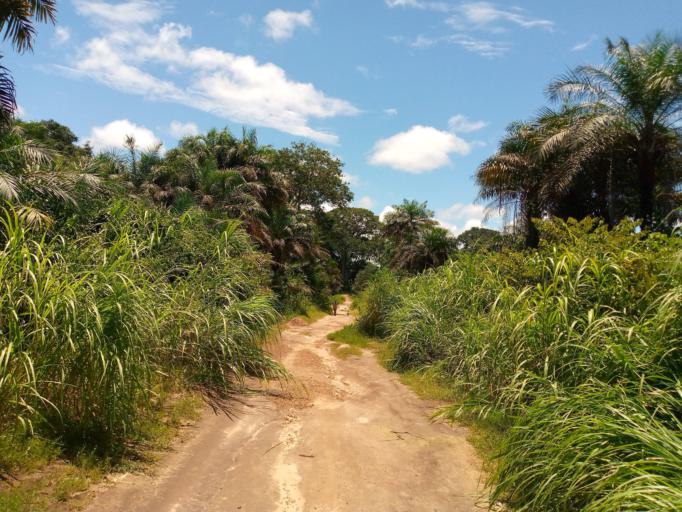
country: SL
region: Northern Province
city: Makeni
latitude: 9.0368
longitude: -12.1591
